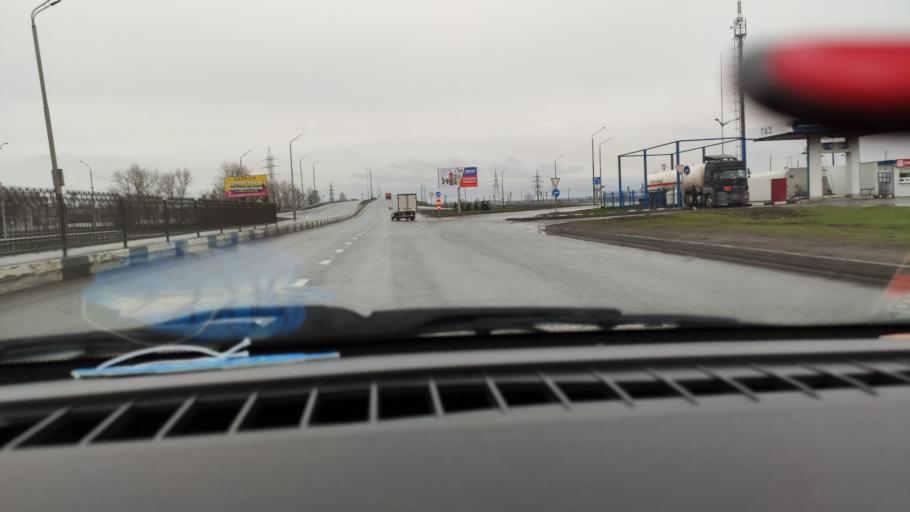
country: RU
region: Tatarstan
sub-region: Tukayevskiy Rayon
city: Naberezhnyye Chelny
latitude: 55.6668
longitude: 52.2709
